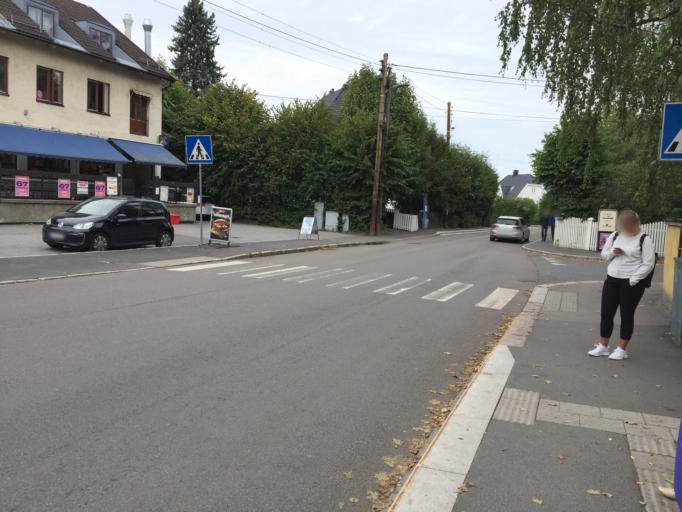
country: NO
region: Oslo
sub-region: Oslo
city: Sjolyststranda
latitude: 59.9032
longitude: 10.6869
